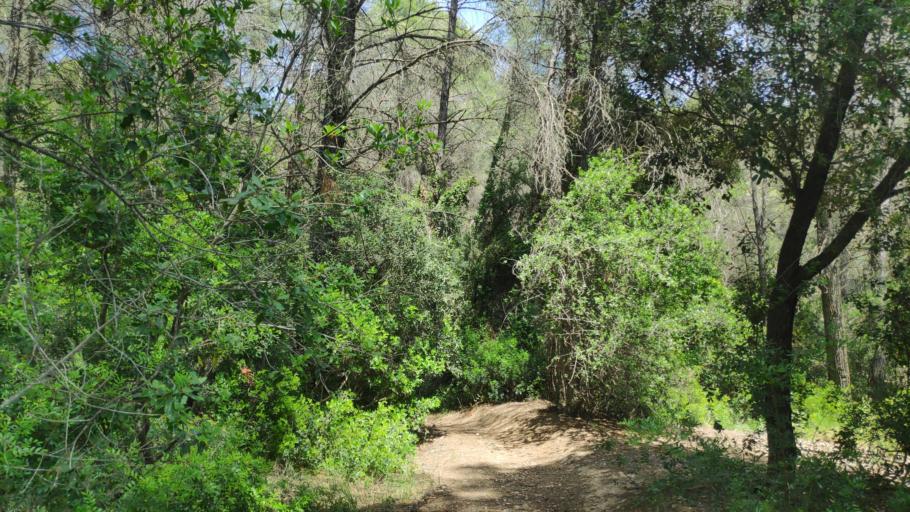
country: ES
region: Catalonia
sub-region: Provincia de Barcelona
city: Rubi
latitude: 41.5044
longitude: 2.0595
